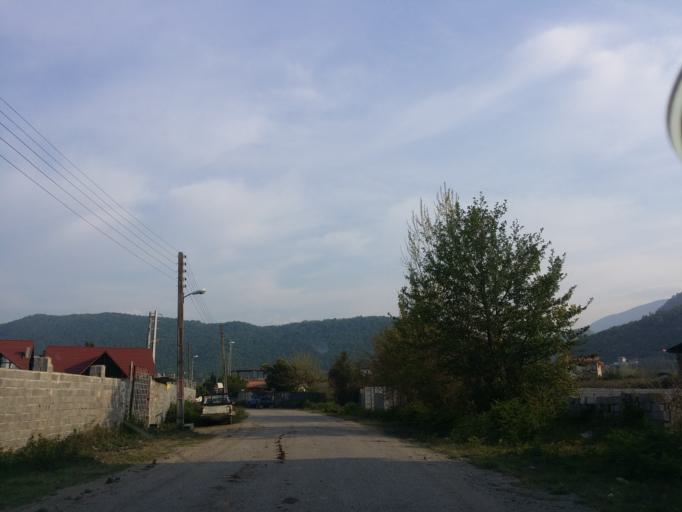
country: IR
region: Mazandaran
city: Chalus
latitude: 36.6596
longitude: 51.3669
